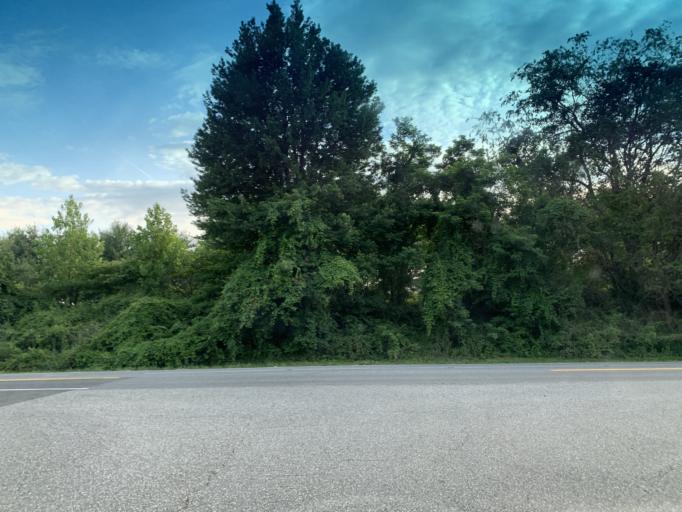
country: US
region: Maryland
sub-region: Harford County
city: Bel Air North
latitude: 39.5686
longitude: -76.3776
